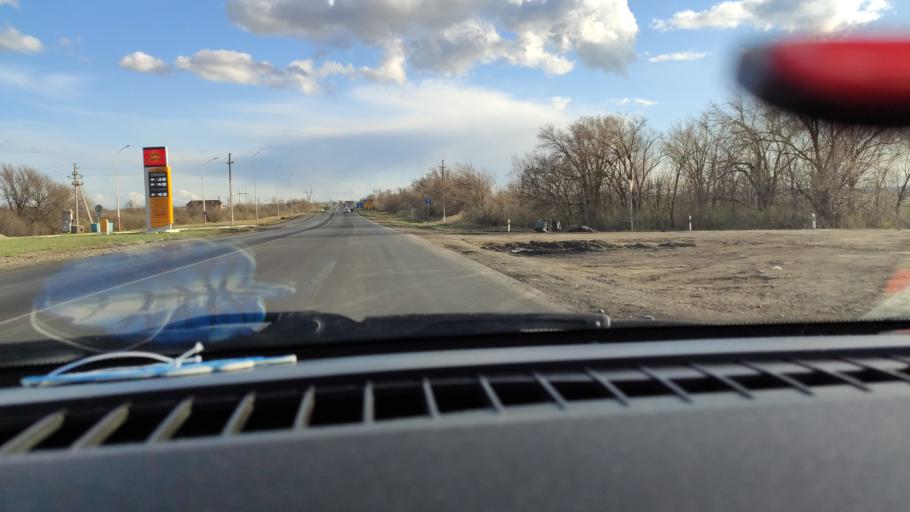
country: RU
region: Saratov
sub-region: Saratovskiy Rayon
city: Saratov
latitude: 51.6770
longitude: 46.0010
